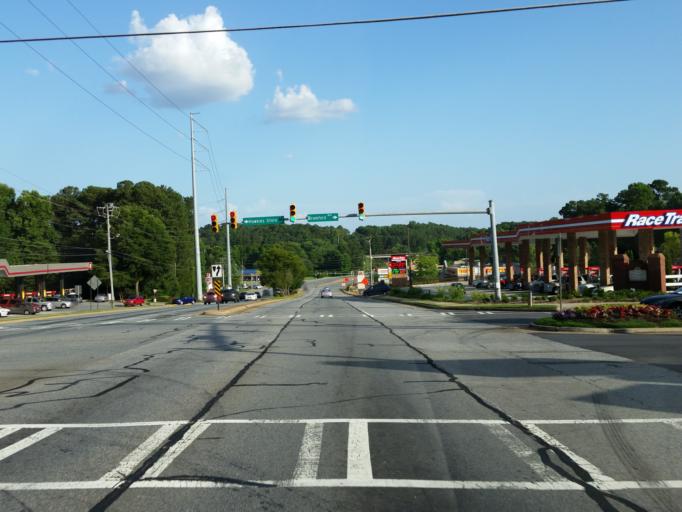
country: US
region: Georgia
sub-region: Cherokee County
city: Woodstock
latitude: 34.0580
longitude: -84.5578
